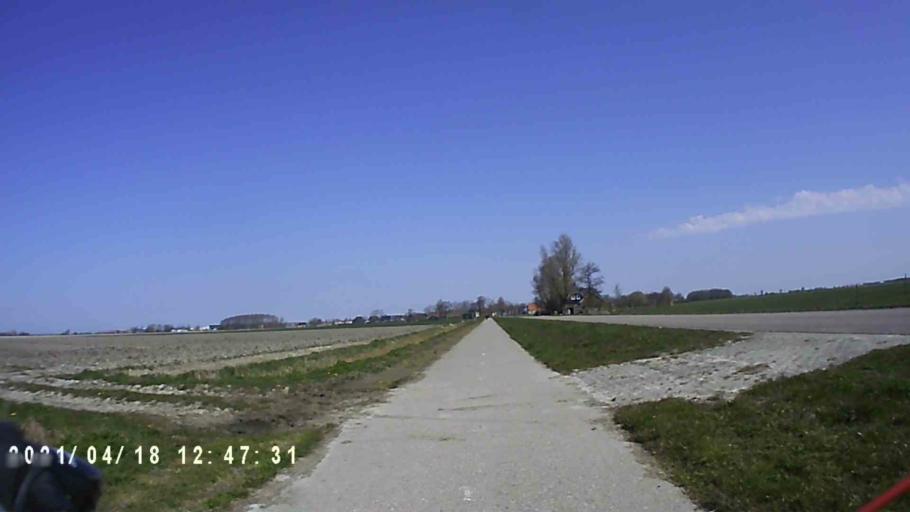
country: NL
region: Friesland
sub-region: Gemeente Dongeradeel
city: Dokkum
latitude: 53.3704
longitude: 6.0497
